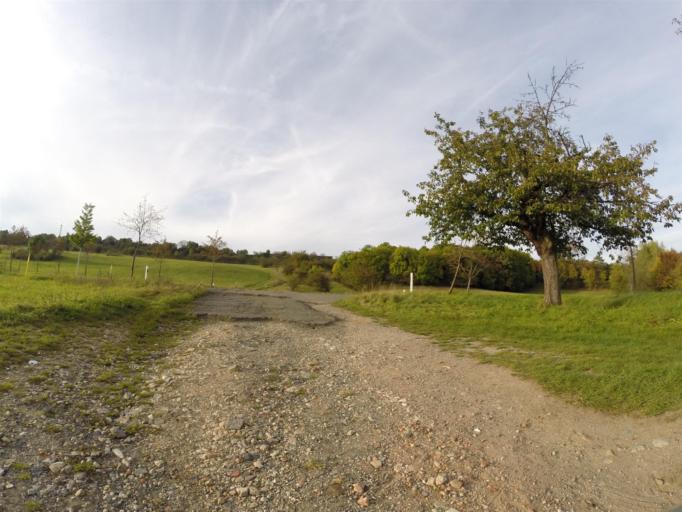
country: DE
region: Thuringia
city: Lehesten
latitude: 50.9622
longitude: 11.6038
